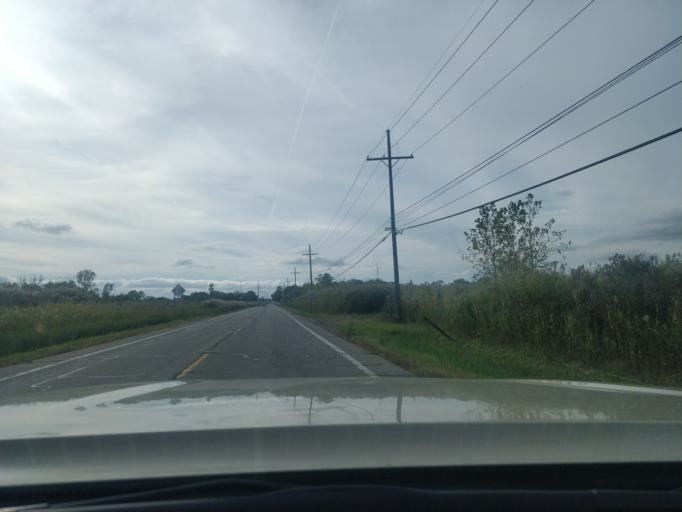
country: US
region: Michigan
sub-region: Wayne County
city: Romulus
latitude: 42.1802
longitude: -83.3654
